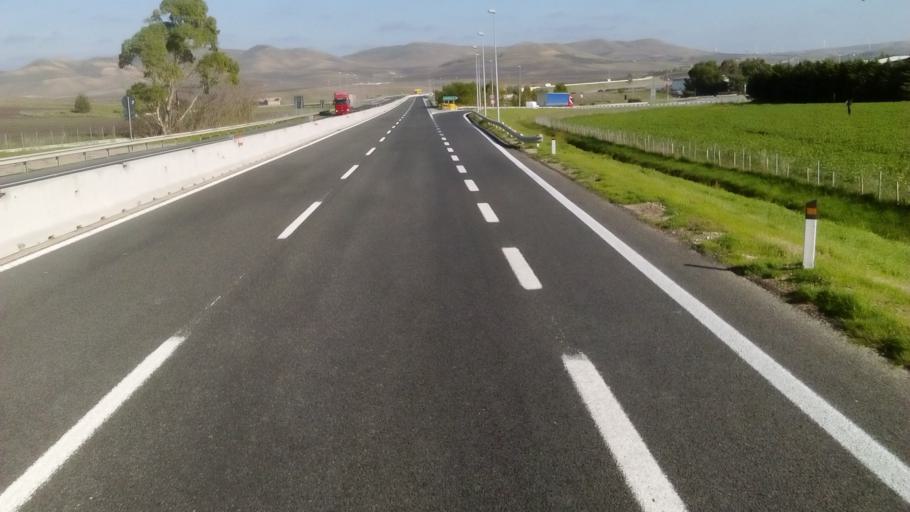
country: IT
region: Apulia
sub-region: Provincia di Foggia
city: Candela
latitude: 41.1506
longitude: 15.5226
